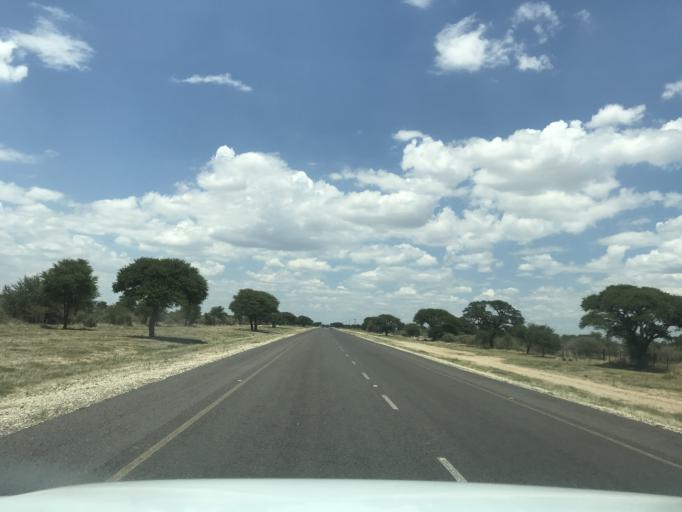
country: BW
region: South East
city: Janeng
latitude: -25.6324
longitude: 25.1542
